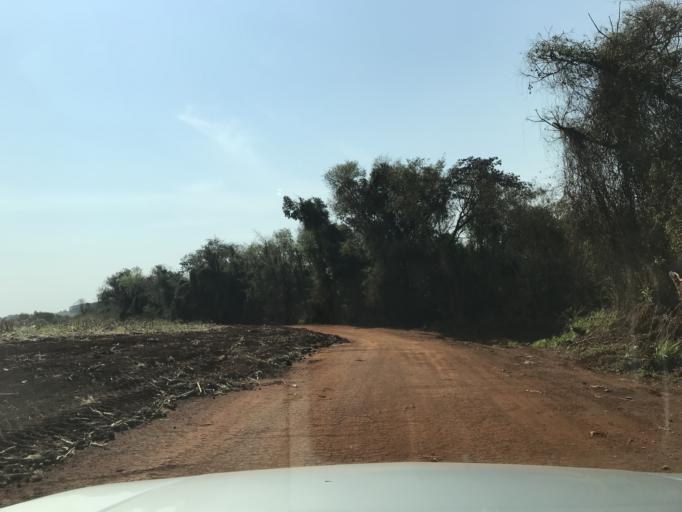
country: BR
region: Parana
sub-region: Palotina
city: Palotina
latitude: -24.2194
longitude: -53.7342
